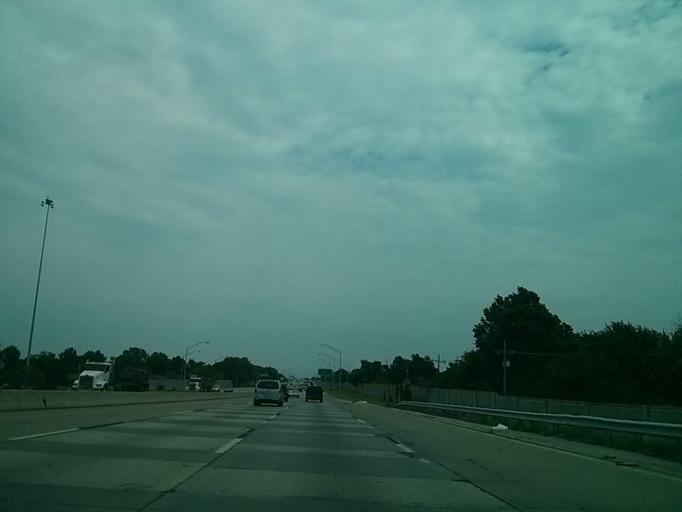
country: US
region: Oklahoma
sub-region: Tulsa County
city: Broken Arrow
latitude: 36.1201
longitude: -95.8595
